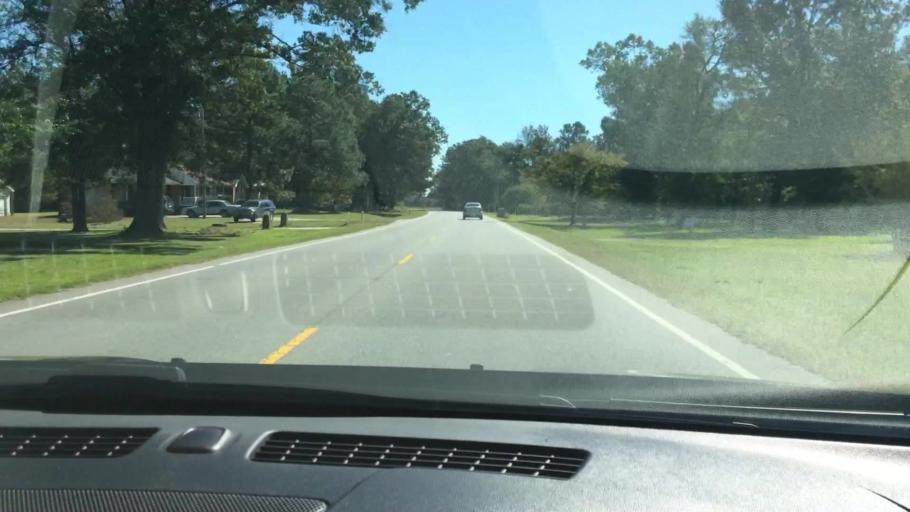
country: US
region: North Carolina
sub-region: Pitt County
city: Grifton
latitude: 35.3549
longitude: -77.3383
